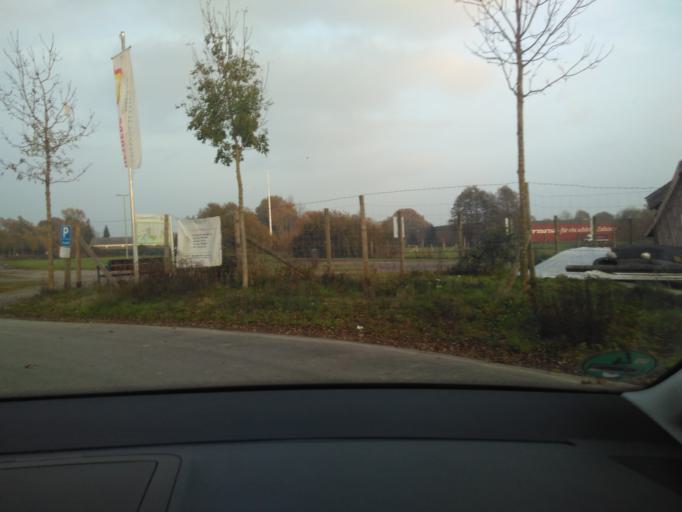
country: DE
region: North Rhine-Westphalia
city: Rietberg
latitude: 51.8176
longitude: 8.4428
